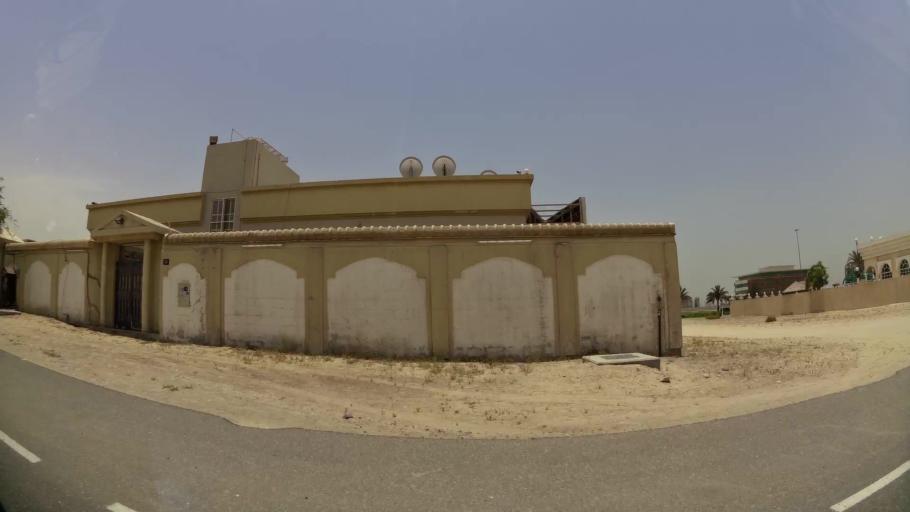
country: AE
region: Ash Shariqah
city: Sharjah
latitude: 25.2089
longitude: 55.3775
